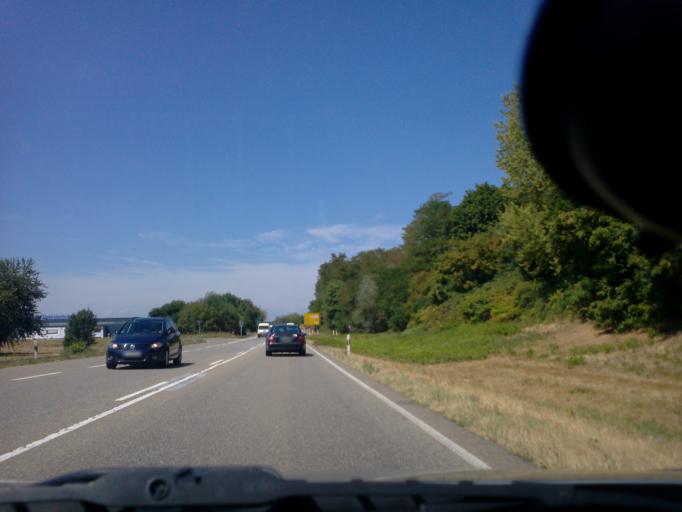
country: DE
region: Baden-Wuerttemberg
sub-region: Freiburg Region
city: Offenburg
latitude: 48.4476
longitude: 7.9396
